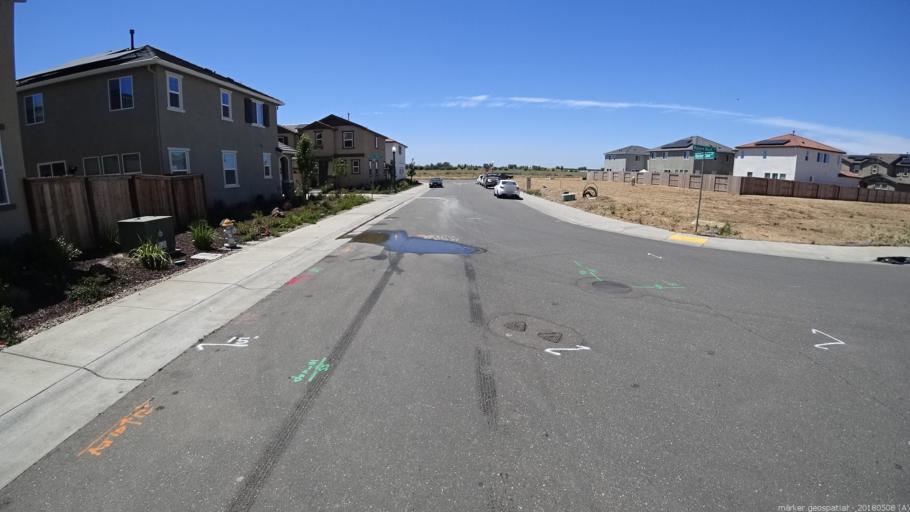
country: US
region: California
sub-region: Sacramento County
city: Elverta
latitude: 38.6681
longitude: -121.5295
